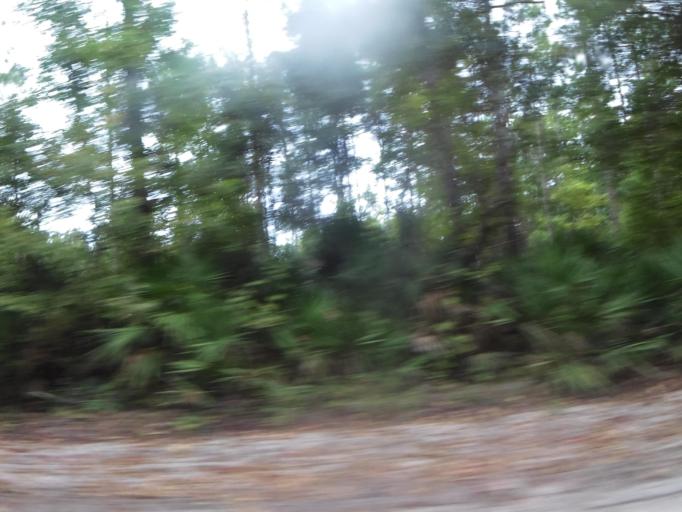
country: US
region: Florida
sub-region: Flagler County
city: Palm Coast
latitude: 29.6276
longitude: -81.3700
